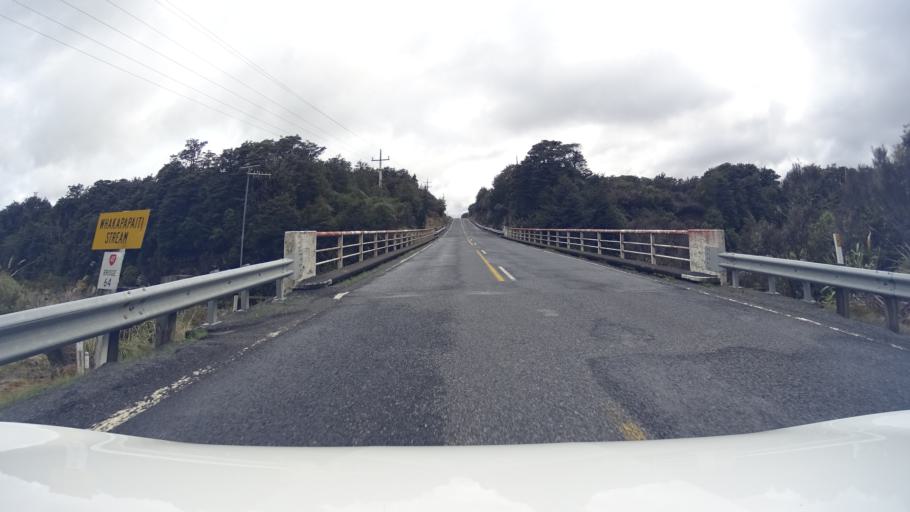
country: NZ
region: Manawatu-Wanganui
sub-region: Ruapehu District
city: Waiouru
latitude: -39.1755
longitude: 175.4719
